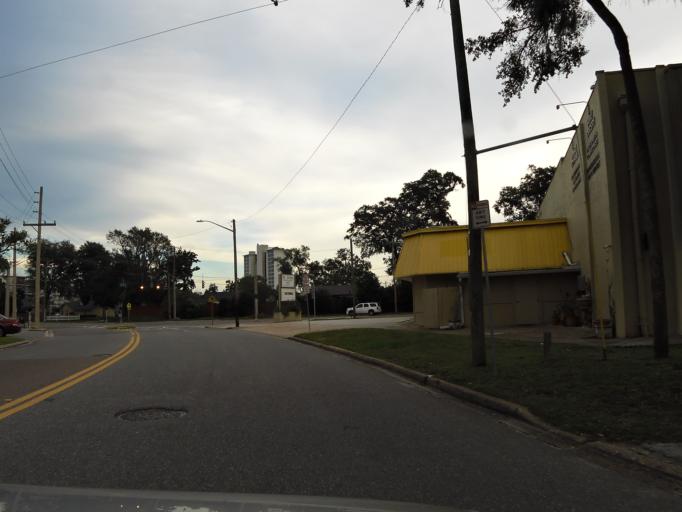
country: US
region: Florida
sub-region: Duval County
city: Jacksonville
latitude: 30.2885
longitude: -81.7141
